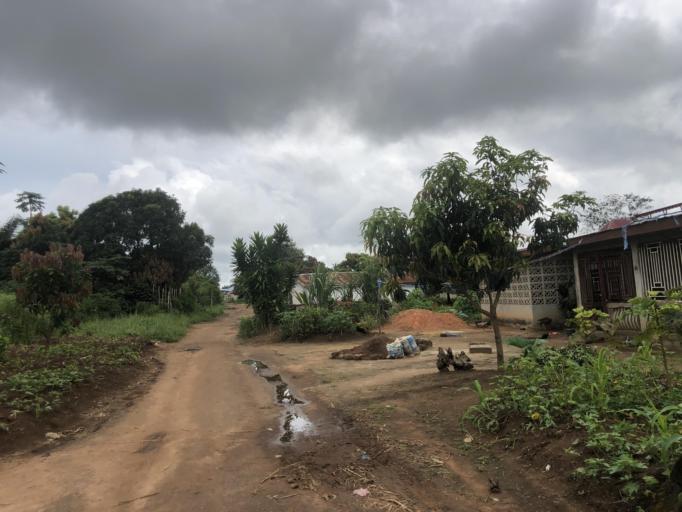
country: SL
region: Northern Province
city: Makeni
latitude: 8.9075
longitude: -12.0411
